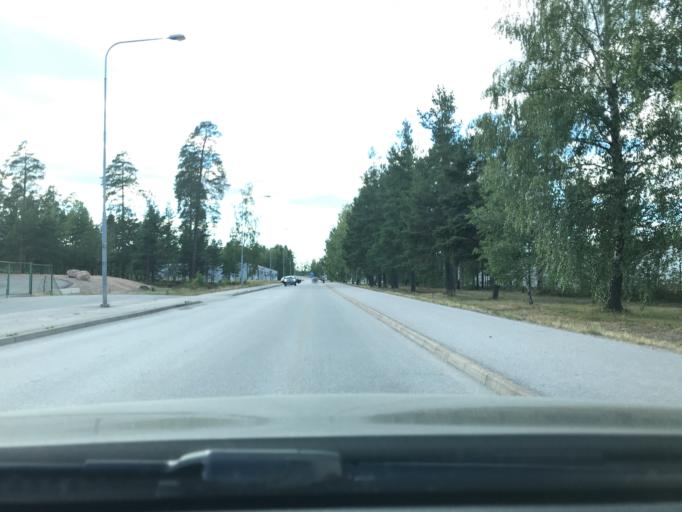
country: SE
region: Kalmar
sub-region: Hultsfreds Kommun
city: Hultsfred
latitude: 57.4973
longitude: 15.8301
